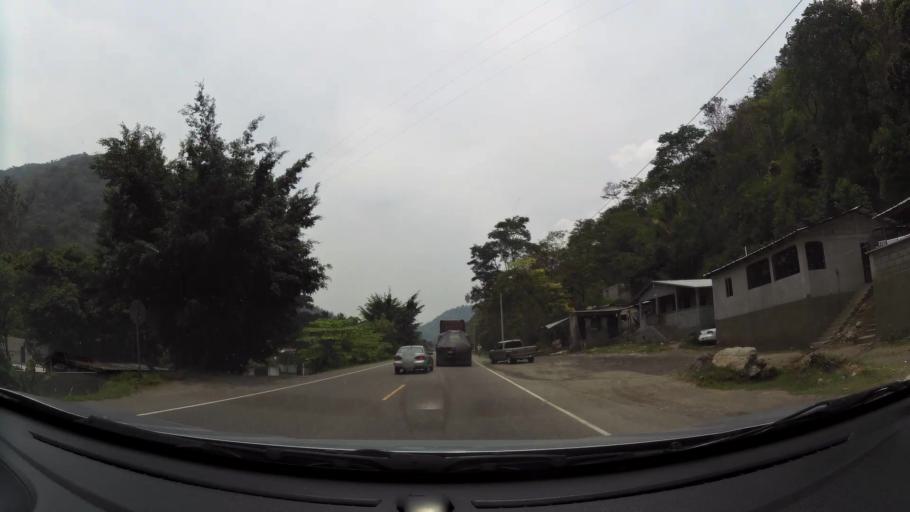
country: HN
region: Comayagua
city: Taulabe
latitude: 14.7408
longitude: -87.9637
